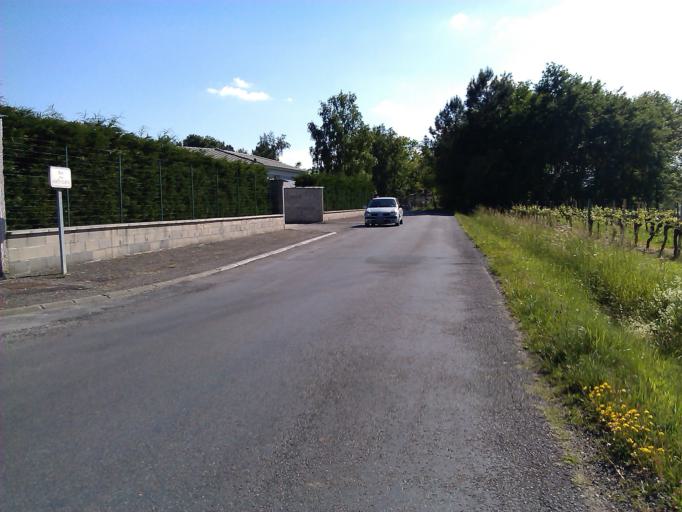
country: FR
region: Aquitaine
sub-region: Departement de la Gironde
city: Cezac
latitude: 45.0799
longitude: -0.4023
